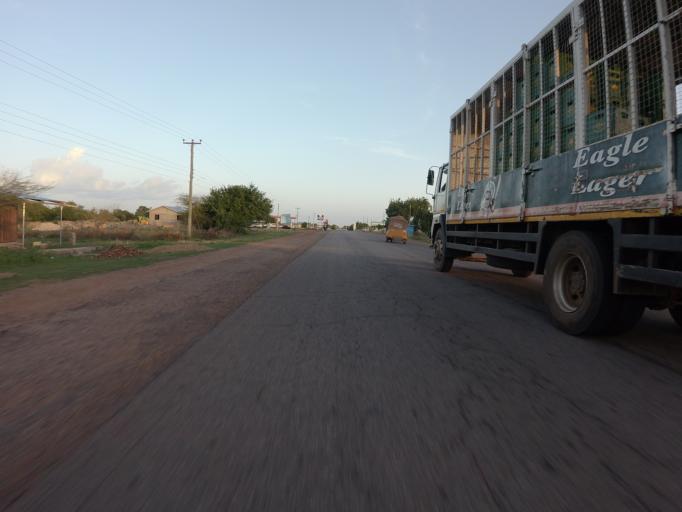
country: GH
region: Upper East
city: Navrongo
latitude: 10.9594
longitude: -1.0984
